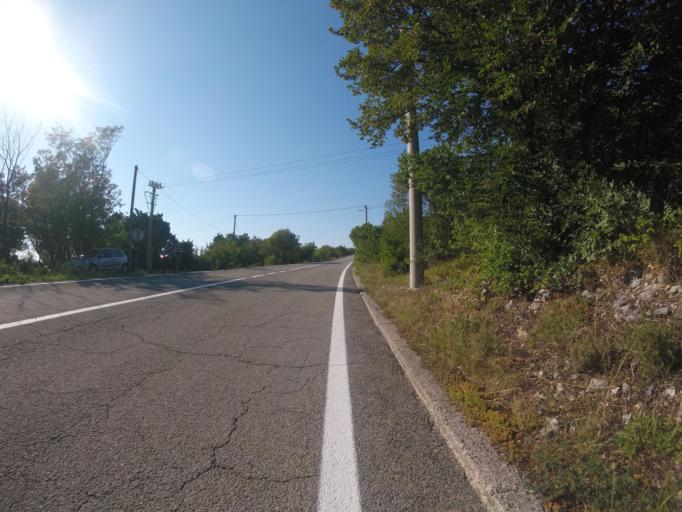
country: HR
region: Primorsko-Goranska
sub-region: Grad Crikvenica
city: Jadranovo
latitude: 45.2477
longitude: 14.6093
